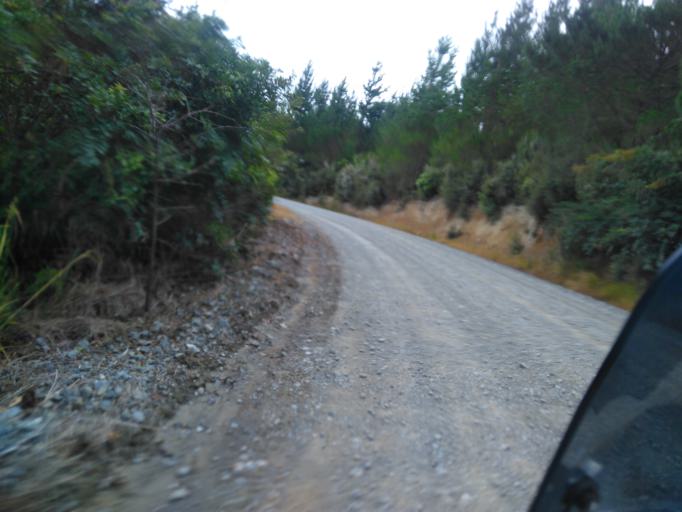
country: NZ
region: Gisborne
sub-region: Gisborne District
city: Gisborne
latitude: -38.1535
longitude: 178.1315
